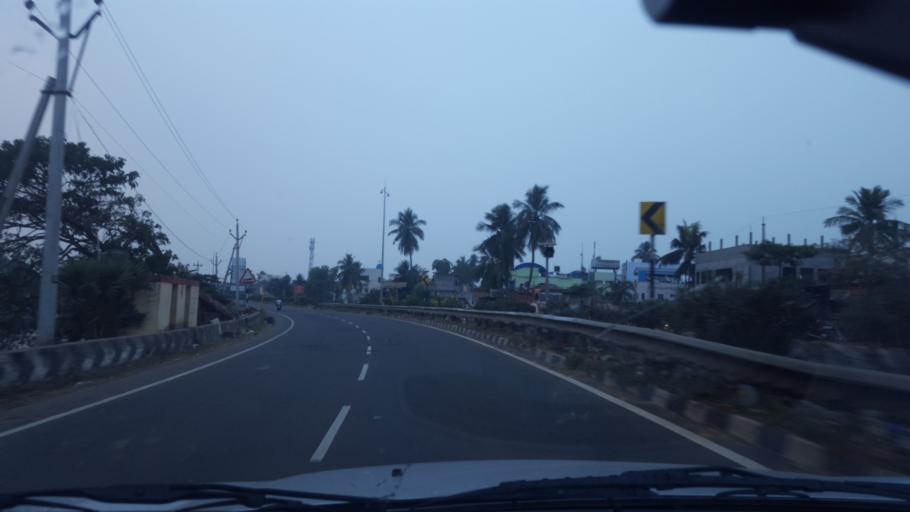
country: IN
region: Andhra Pradesh
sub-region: East Godavari
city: Rajahmundry
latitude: 16.8860
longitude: 81.8084
